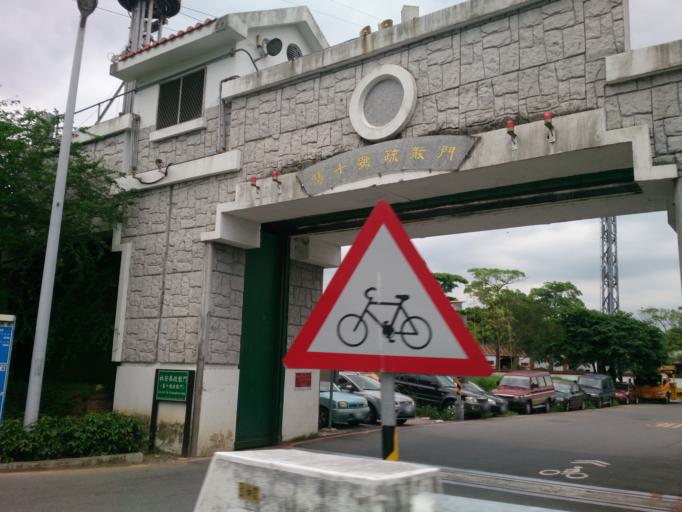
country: TW
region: Taipei
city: Taipei
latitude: 25.0730
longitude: 121.5294
